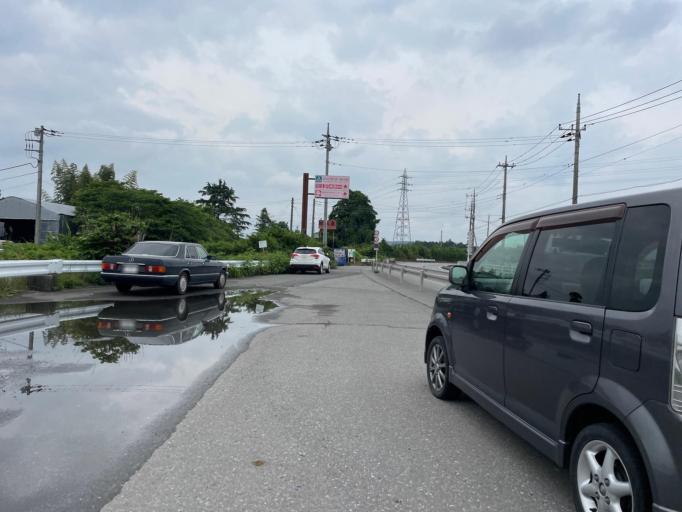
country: JP
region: Tochigi
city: Kanuma
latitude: 36.4785
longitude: 139.7512
